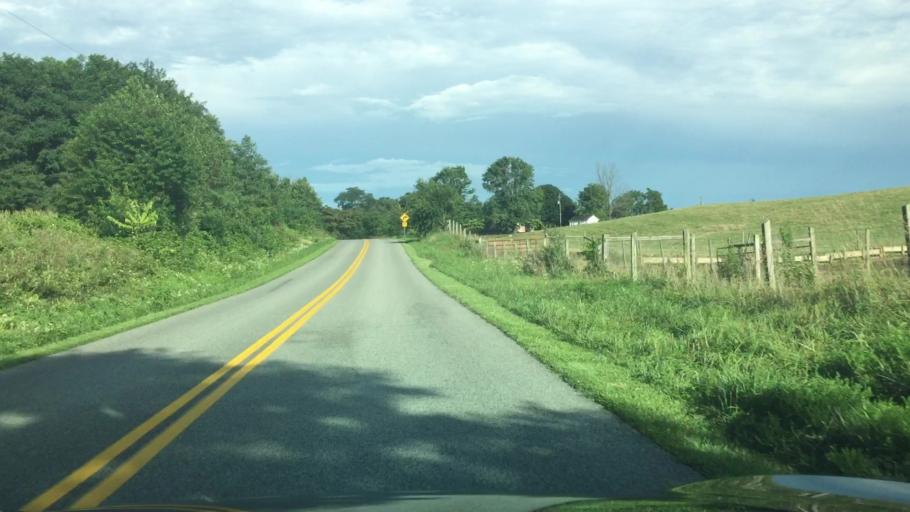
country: US
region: Virginia
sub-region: Wythe County
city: Wytheville
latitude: 36.9371
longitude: -80.9511
